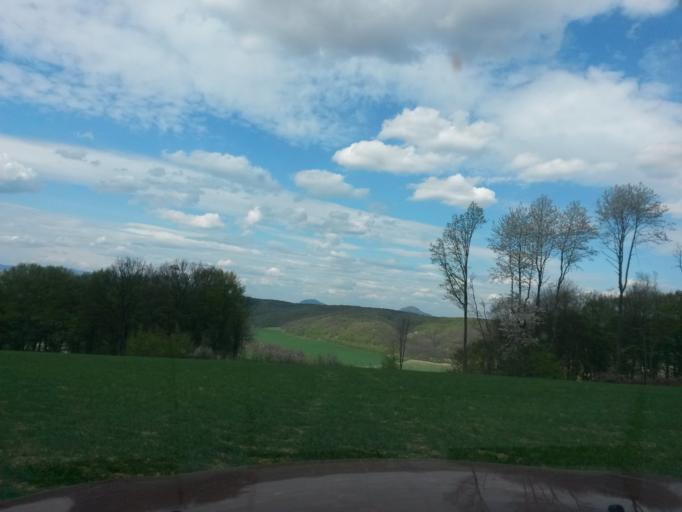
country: SK
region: Presovsky
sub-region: Okres Presov
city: Presov
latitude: 48.9552
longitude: 21.1285
